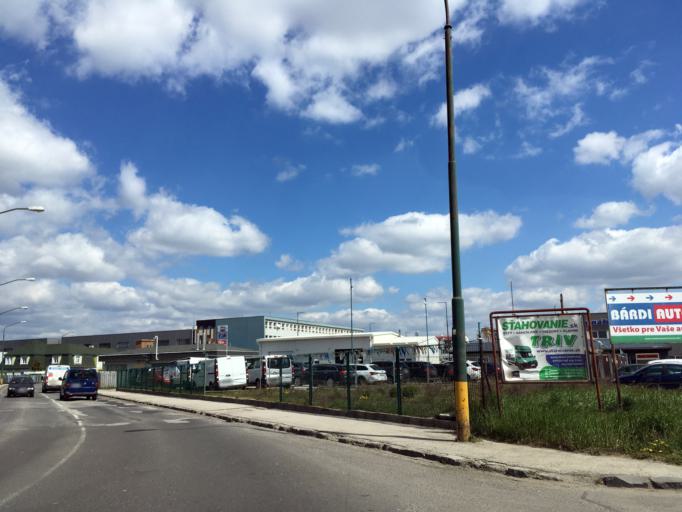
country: SK
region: Bratislavsky
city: Bratislava
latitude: 48.1843
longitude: 17.1640
